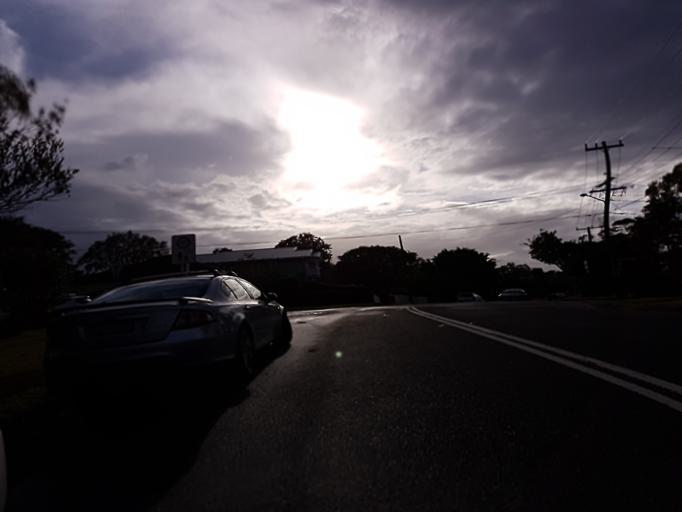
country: AU
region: New South Wales
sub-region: Warringah
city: Allambie Heights
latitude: -33.7807
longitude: 151.2387
